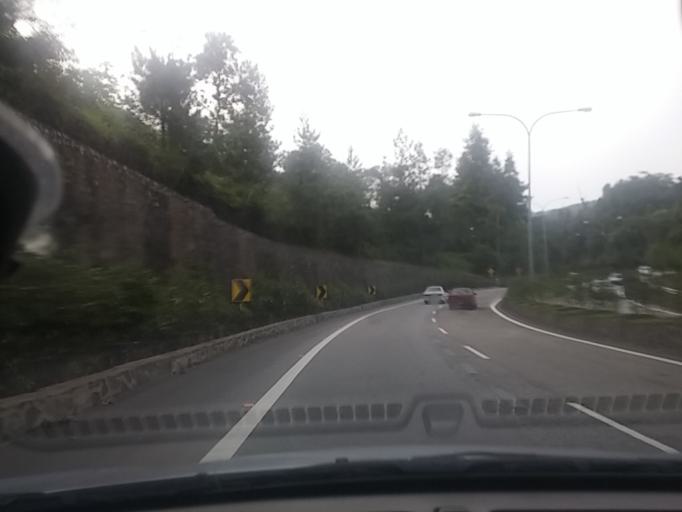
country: MY
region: Pahang
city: Kampung Bukit Tinggi, Bentong
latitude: 3.3946
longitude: 101.7693
